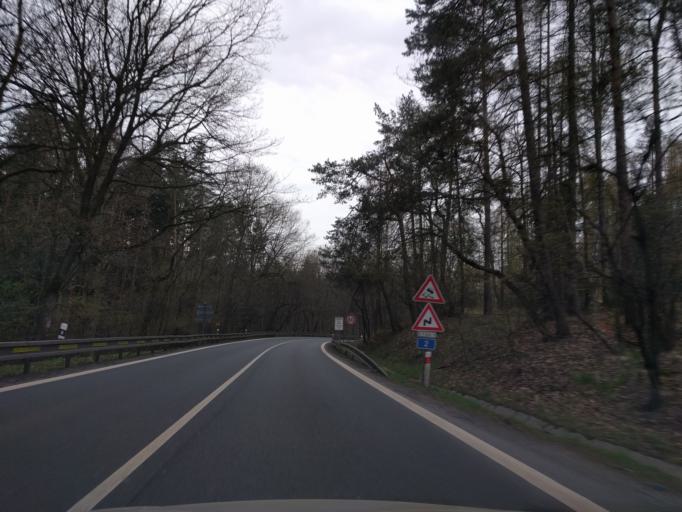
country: CZ
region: Central Bohemia
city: Mukarov
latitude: 49.9880
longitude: 14.7060
